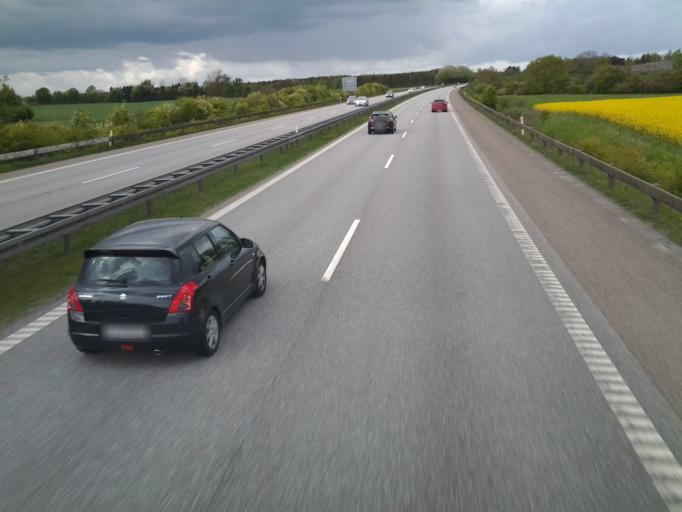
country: DK
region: Zealand
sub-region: Vordingborg Kommune
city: Orslev
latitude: 55.1395
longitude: 11.9373
